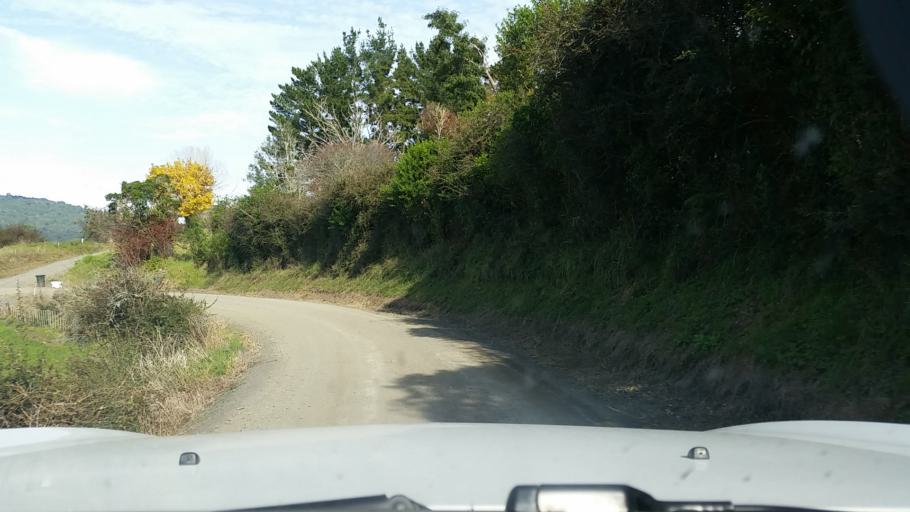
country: NZ
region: Waikato
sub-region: Matamata-Piako District
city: Matamata
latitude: -37.8065
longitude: 175.6352
